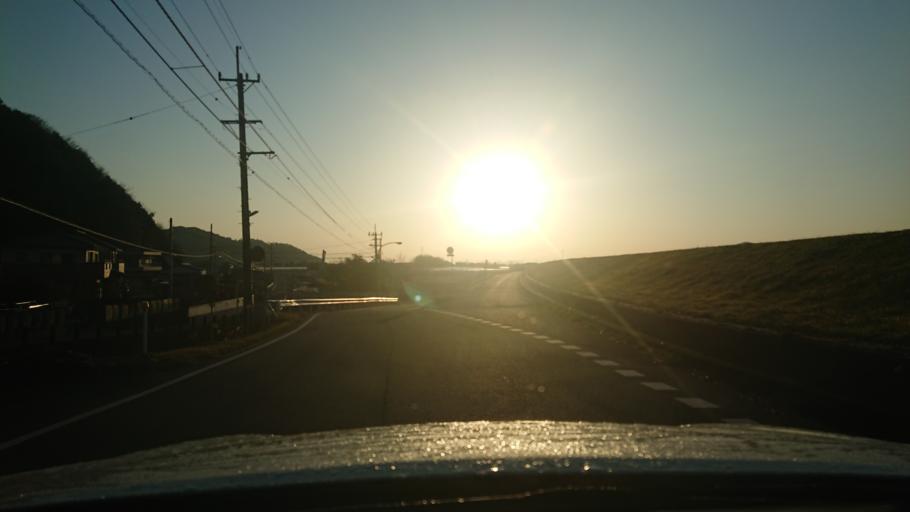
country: JP
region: Tokushima
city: Komatsushimacho
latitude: 33.9437
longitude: 134.5885
